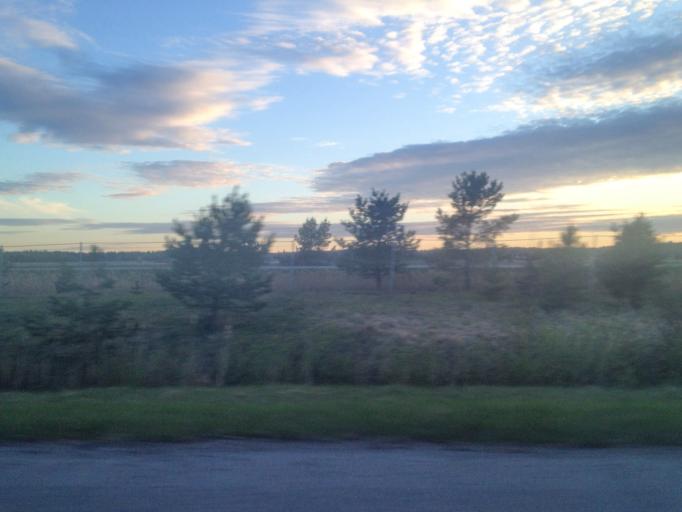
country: FI
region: Uusimaa
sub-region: Helsinki
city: Nurmijaervi
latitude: 60.5235
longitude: 24.8441
